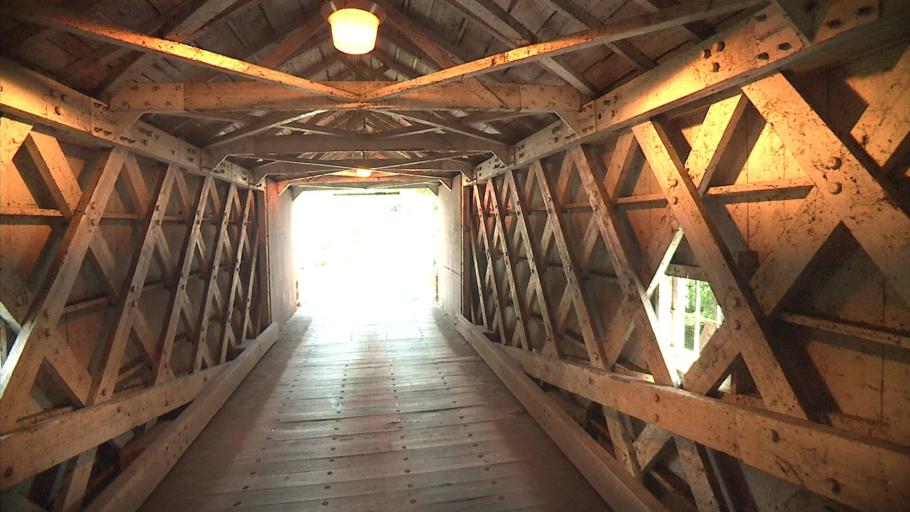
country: US
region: Connecticut
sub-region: Litchfield County
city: Canaan
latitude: 41.8716
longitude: -73.3636
